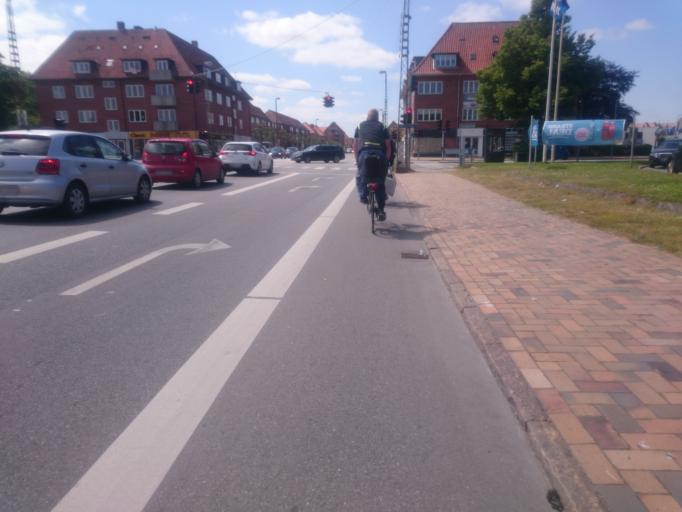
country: DK
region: South Denmark
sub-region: Odense Kommune
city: Odense
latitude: 55.3942
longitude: 10.3570
